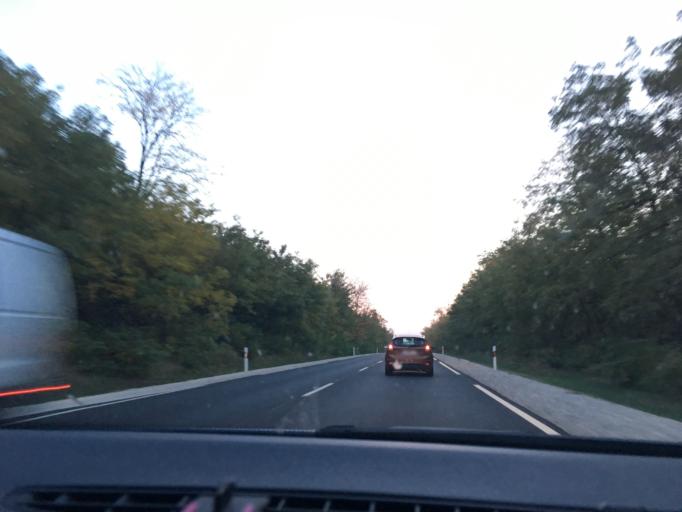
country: HU
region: Hajdu-Bihar
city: Hajduhadhaz
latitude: 47.6077
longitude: 21.6562
